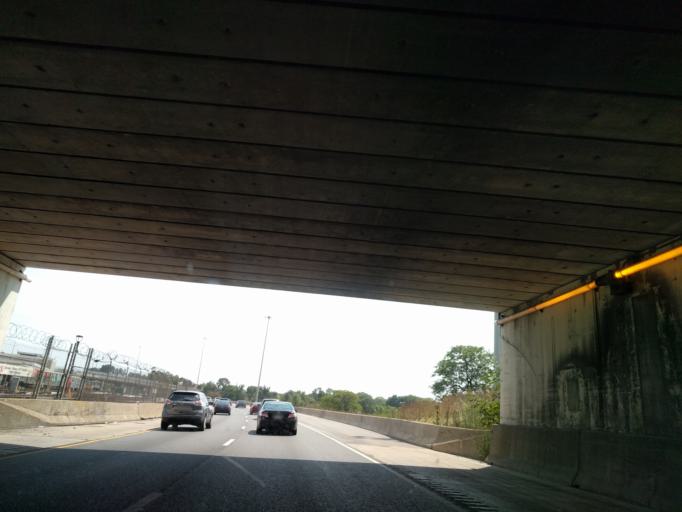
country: US
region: Illinois
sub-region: Cook County
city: Calumet Park
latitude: 41.7175
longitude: -87.6248
